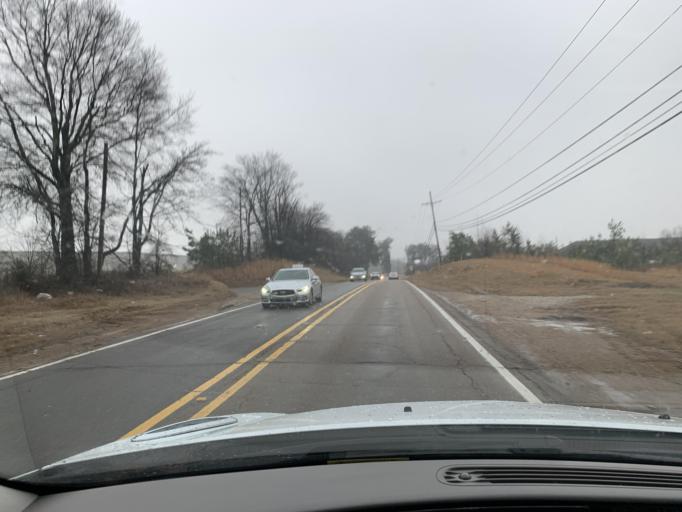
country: US
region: Mississippi
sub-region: De Soto County
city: Horn Lake
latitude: 34.9273
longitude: -90.0109
